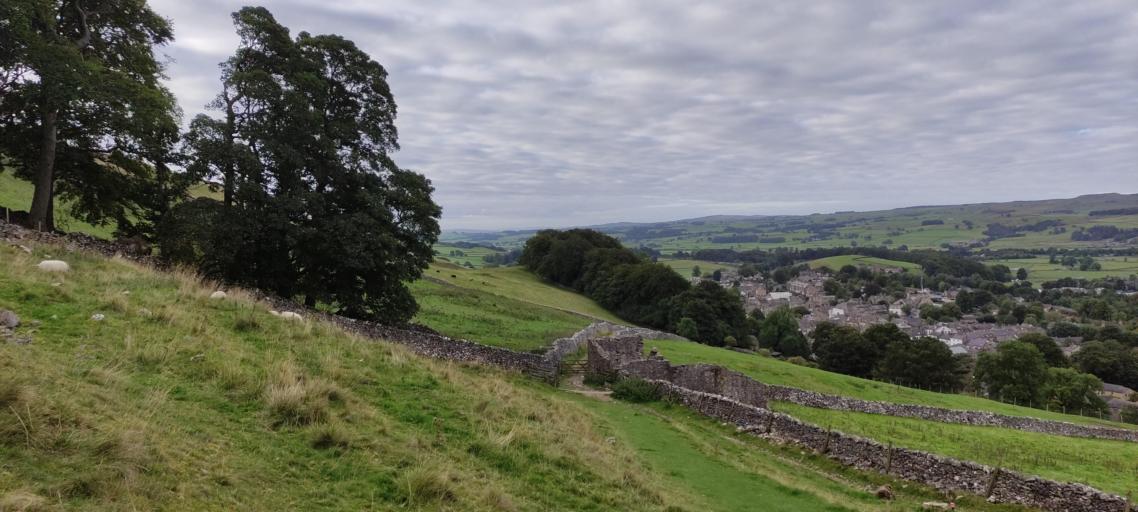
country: GB
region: England
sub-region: North Yorkshire
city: Settle
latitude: 54.0723
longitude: -2.2715
